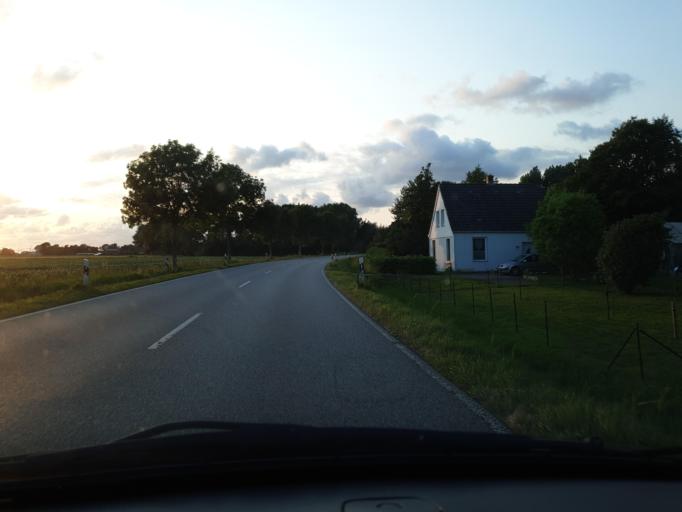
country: DE
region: Schleswig-Holstein
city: Diekhusen-Fahrstedt
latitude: 53.9305
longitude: 9.0352
